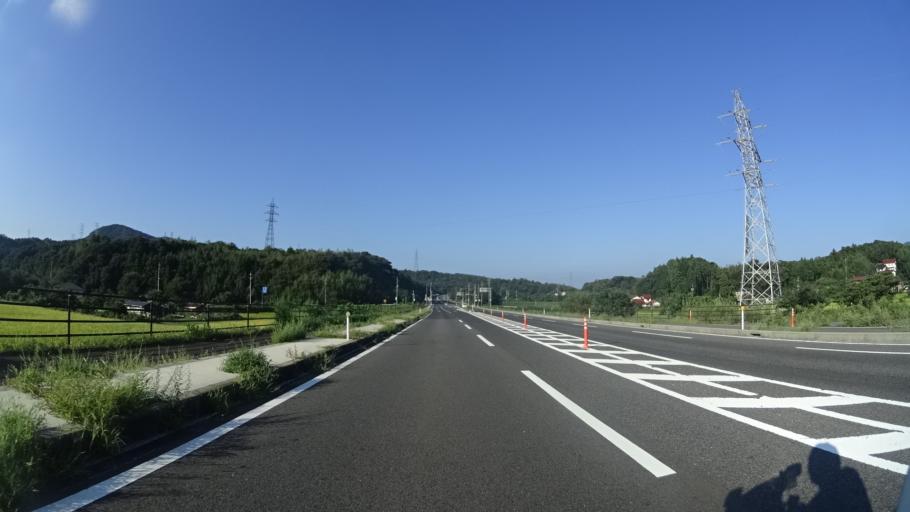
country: JP
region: Shimane
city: Matsue-shi
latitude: 35.5114
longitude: 133.1158
